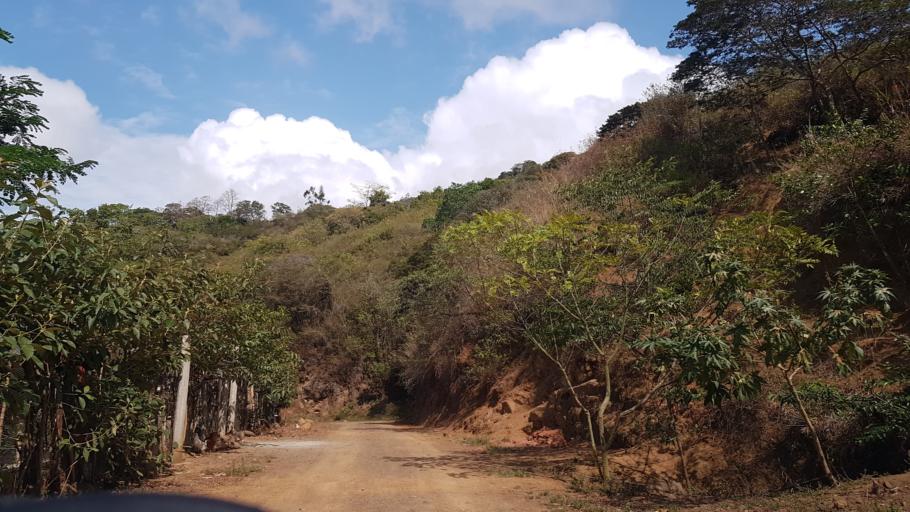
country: CO
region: Valle del Cauca
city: Yumbo
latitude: 3.6527
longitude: -76.5114
